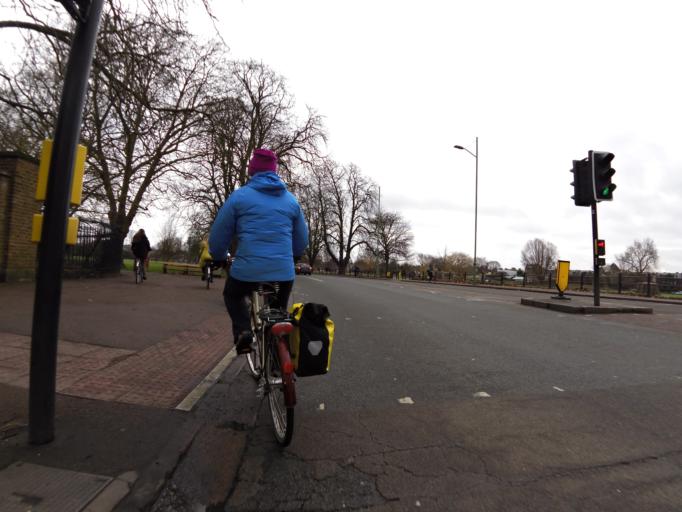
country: GB
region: England
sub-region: Cambridgeshire
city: Cambridge
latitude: 52.2106
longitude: 0.1273
